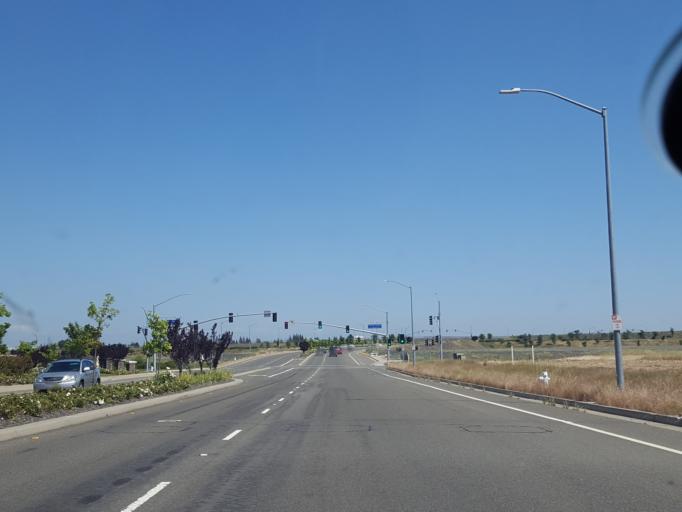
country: US
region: California
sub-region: Sacramento County
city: Rancho Cordova
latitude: 38.5731
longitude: -121.2735
